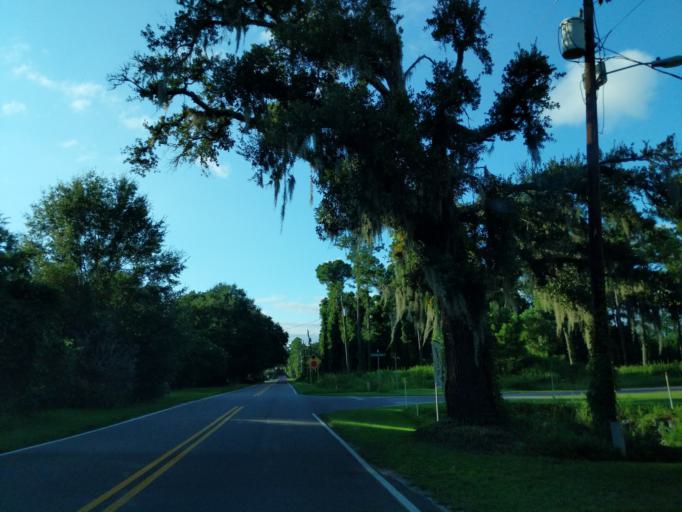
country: US
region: South Carolina
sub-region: Charleston County
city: Awendaw
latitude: 33.0932
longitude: -79.4752
